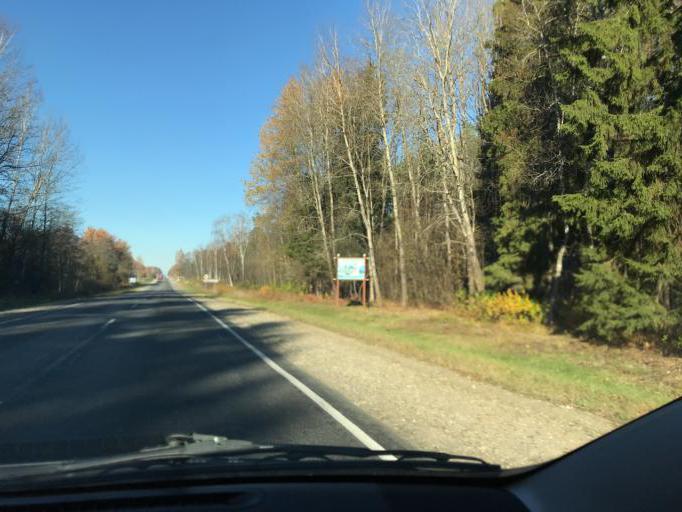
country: BY
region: Vitebsk
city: Polatsk
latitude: 55.5277
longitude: 28.7259
